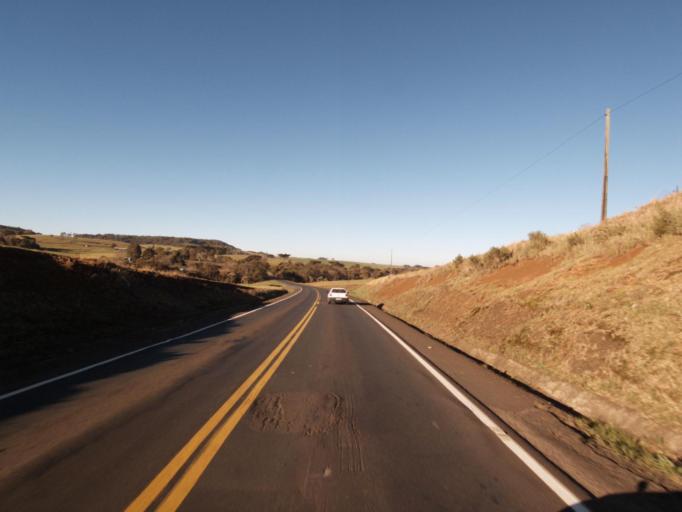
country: AR
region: Misiones
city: Bernardo de Irigoyen
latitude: -26.3404
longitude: -53.5472
